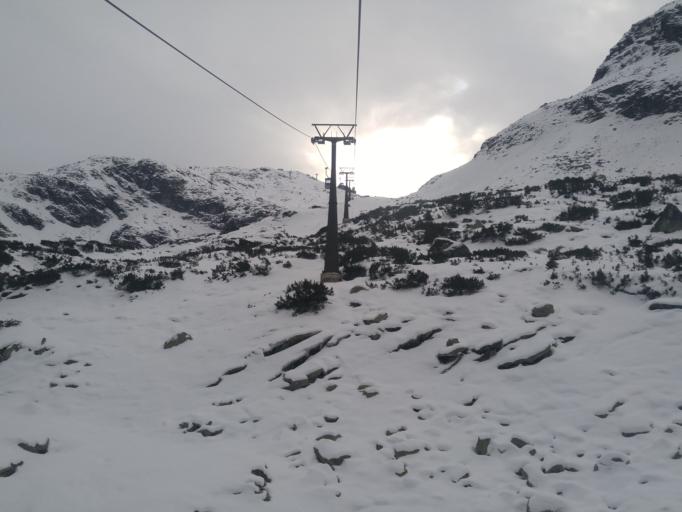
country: AT
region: Salzburg
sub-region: Politischer Bezirk Zell am See
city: Niedernsill
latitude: 47.1501
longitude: 12.6244
